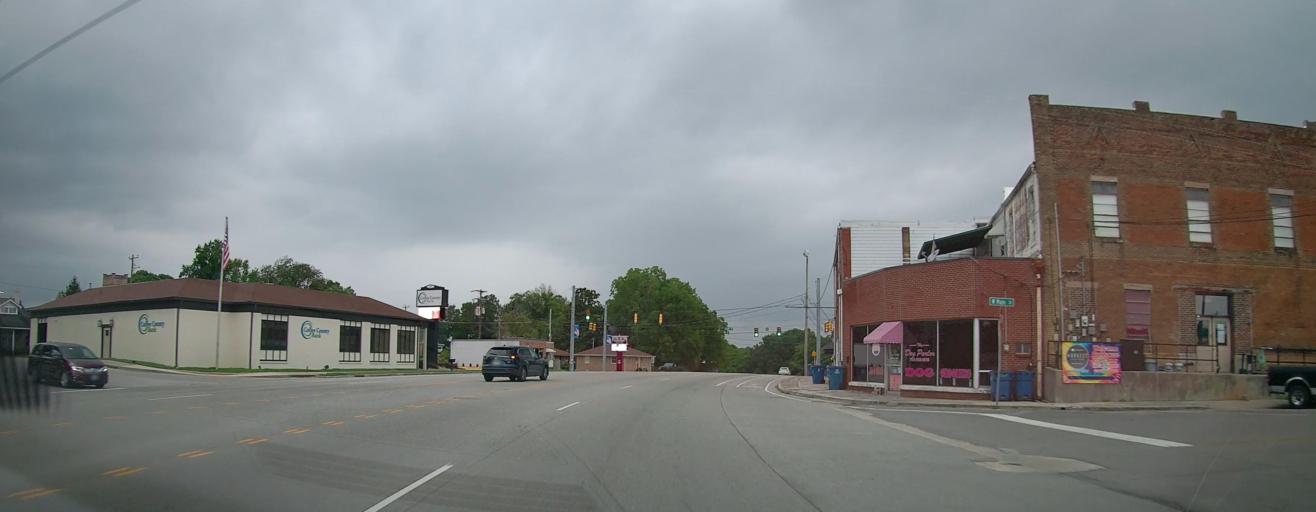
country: US
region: Tennessee
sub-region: Coffee County
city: Manchester
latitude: 35.4828
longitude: -86.0898
